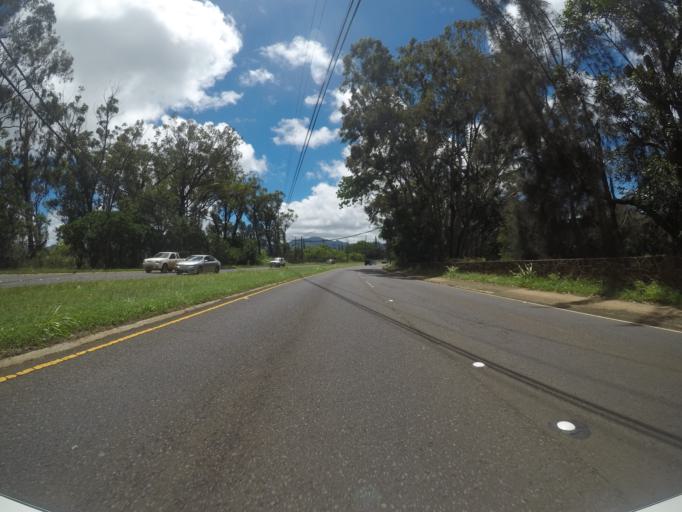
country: US
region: Hawaii
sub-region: Honolulu County
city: Wahiawa
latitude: 21.4889
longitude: -158.0422
